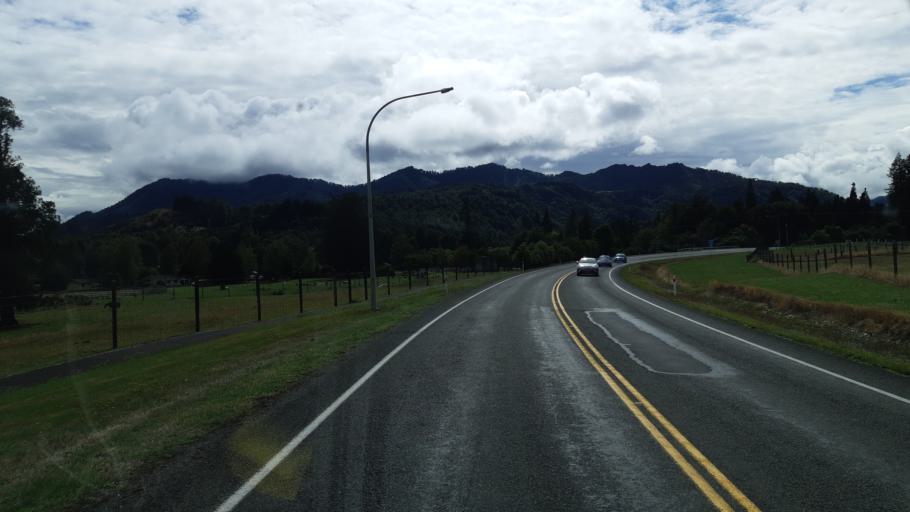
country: NZ
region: West Coast
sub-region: Buller District
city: Westport
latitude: -41.7983
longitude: 172.3376
